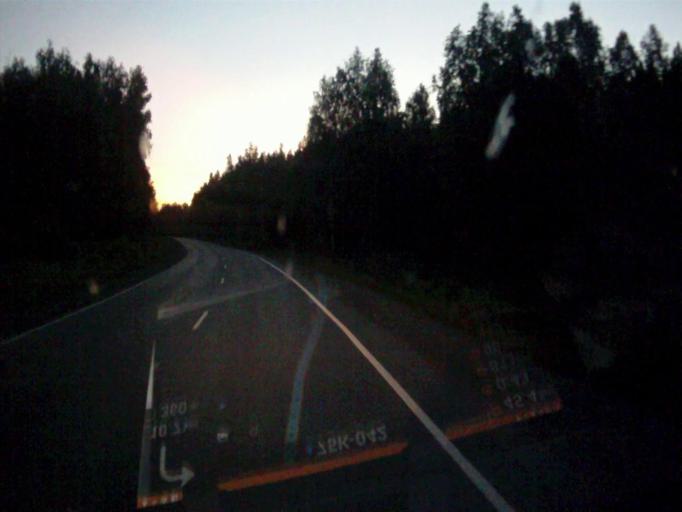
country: RU
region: Chelyabinsk
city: Timiryazevskiy
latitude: 55.2060
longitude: 60.7573
